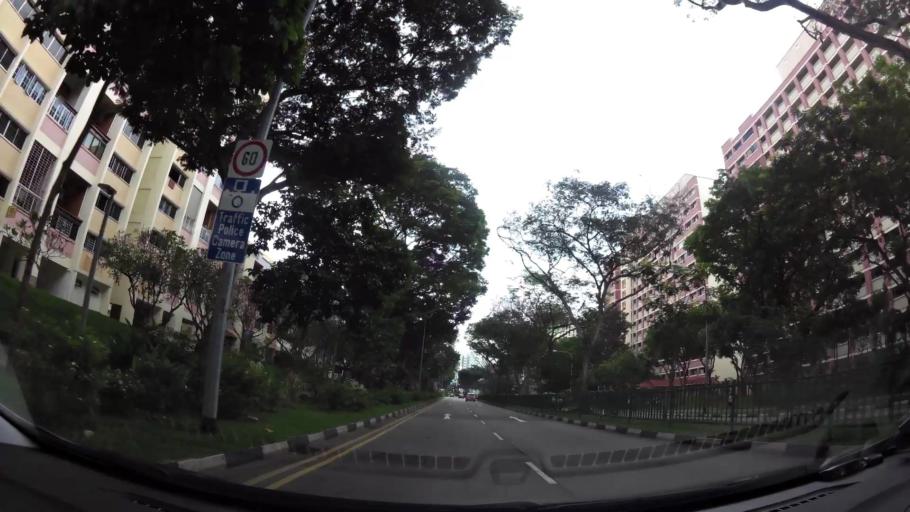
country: SG
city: Singapore
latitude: 1.3557
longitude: 103.9376
